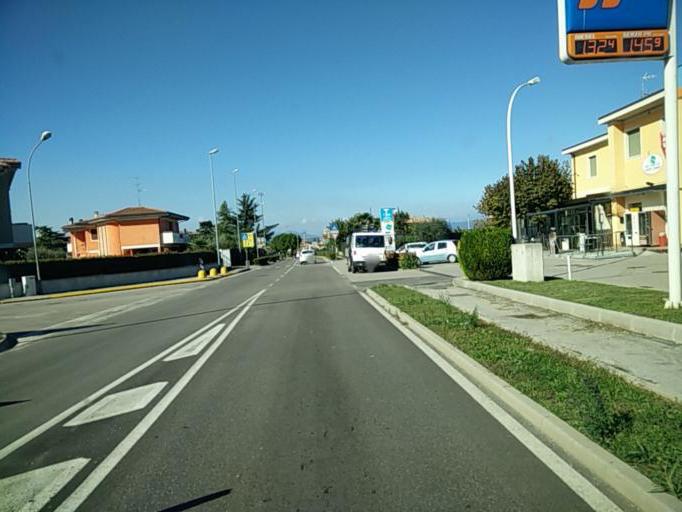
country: IT
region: Lombardy
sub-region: Provincia di Brescia
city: San Martino della Battaglia
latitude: 45.4411
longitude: 10.6007
